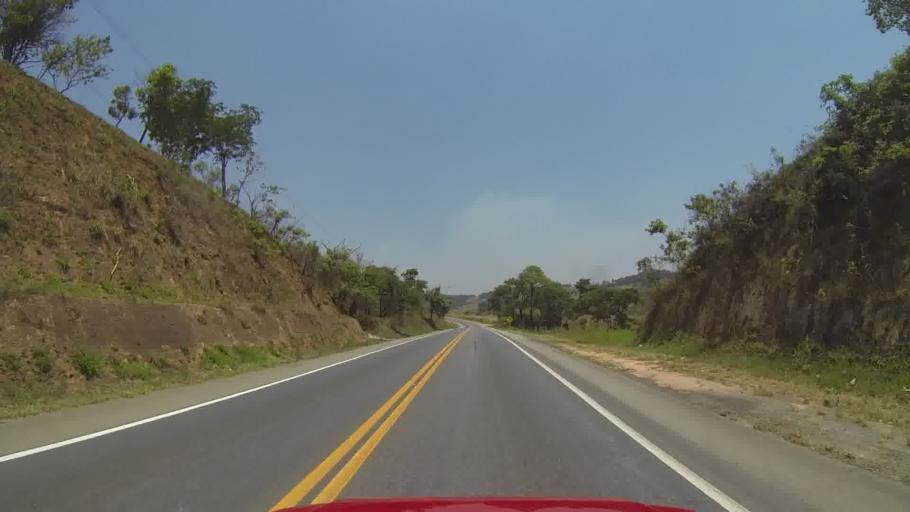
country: BR
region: Minas Gerais
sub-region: Itapecerica
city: Itapecerica
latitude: -20.3282
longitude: -45.2248
